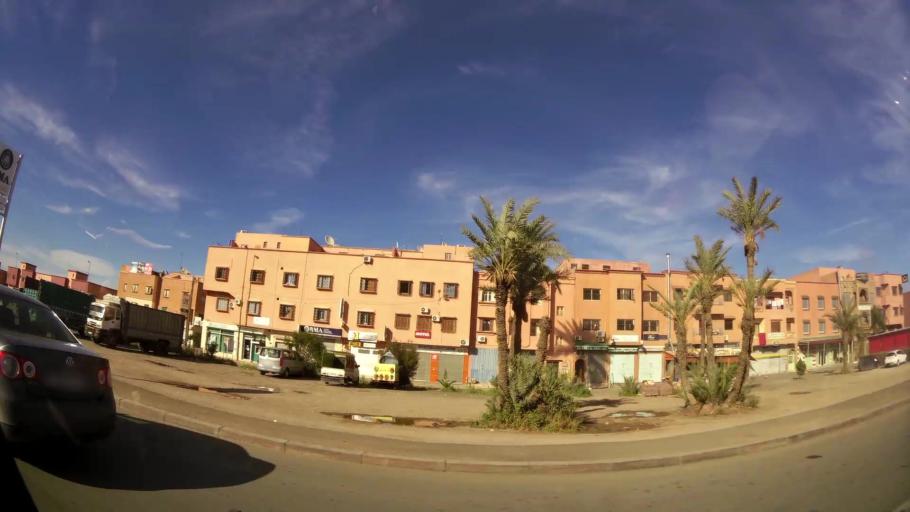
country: MA
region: Marrakech-Tensift-Al Haouz
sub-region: Marrakech
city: Marrakesh
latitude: 31.6708
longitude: -8.0408
